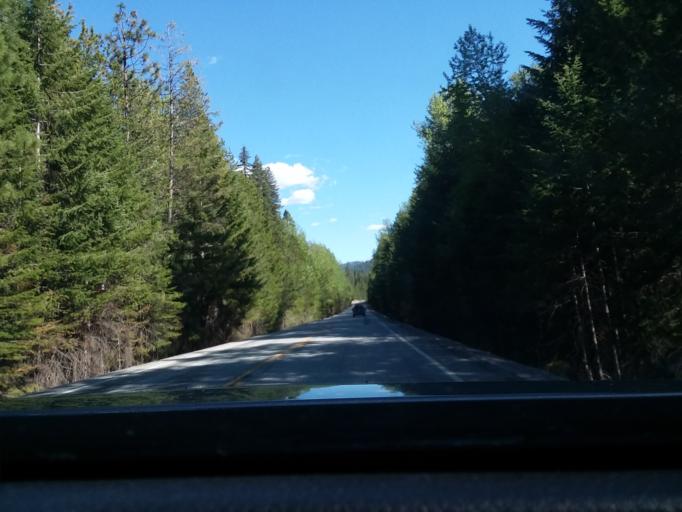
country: US
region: Washington
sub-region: Chelan County
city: Leavenworth
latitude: 47.7991
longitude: -120.6706
